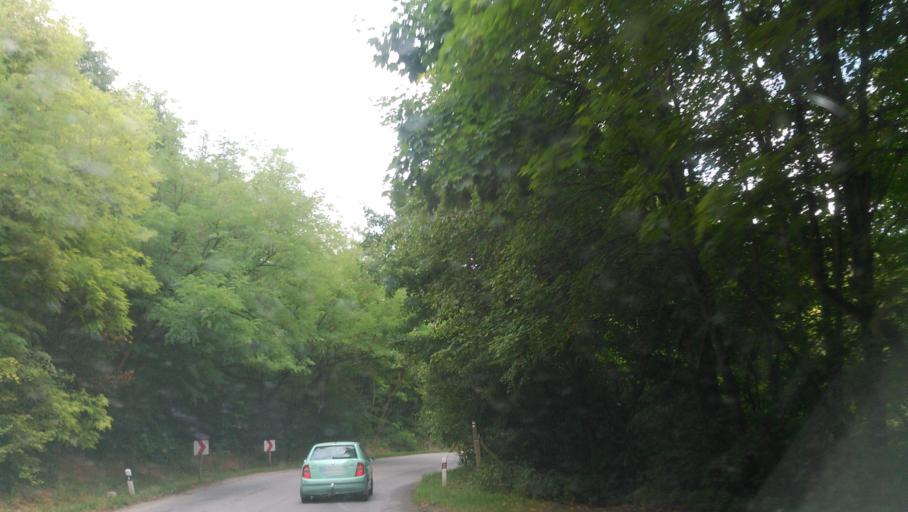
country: SK
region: Trnavsky
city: Hlohovec
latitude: 48.4478
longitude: 17.8183
